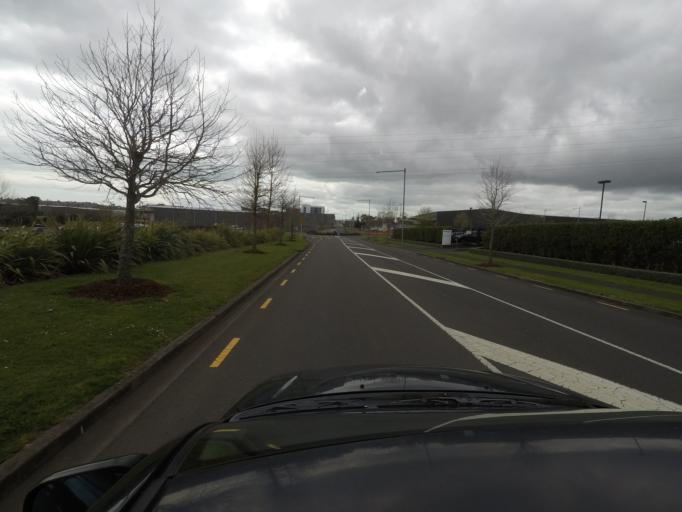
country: NZ
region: Auckland
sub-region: Auckland
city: Tamaki
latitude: -36.9397
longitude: 174.8703
